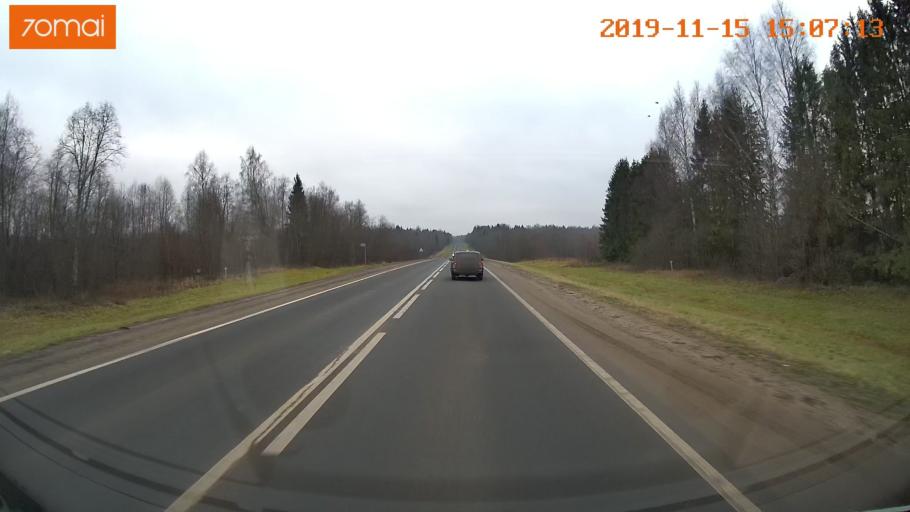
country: RU
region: Jaroslavl
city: Prechistoye
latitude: 58.3859
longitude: 40.2993
